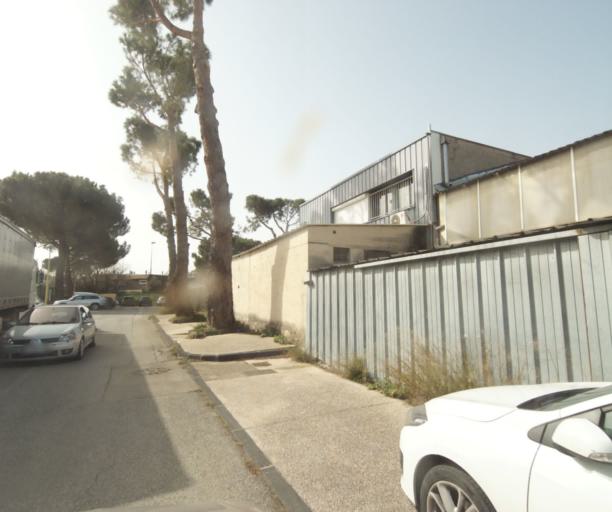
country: FR
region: Provence-Alpes-Cote d'Azur
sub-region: Departement des Bouches-du-Rhone
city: Gardanne
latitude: 43.4634
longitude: 5.4814
